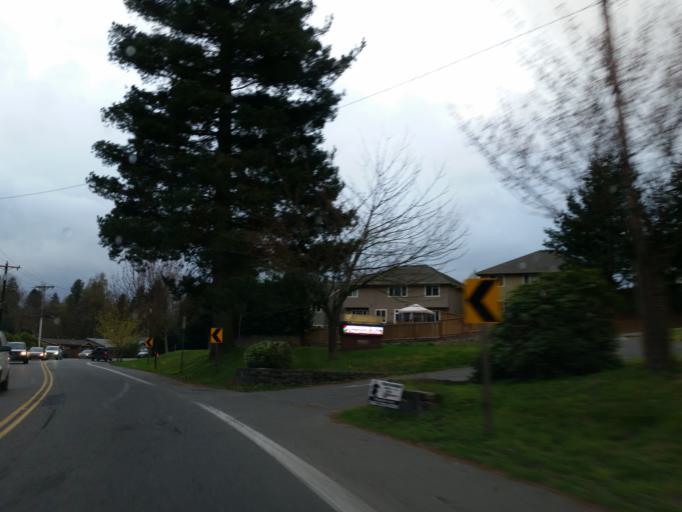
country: US
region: Washington
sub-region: Snohomish County
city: Alderwood Manor
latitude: 47.8084
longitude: -122.2769
